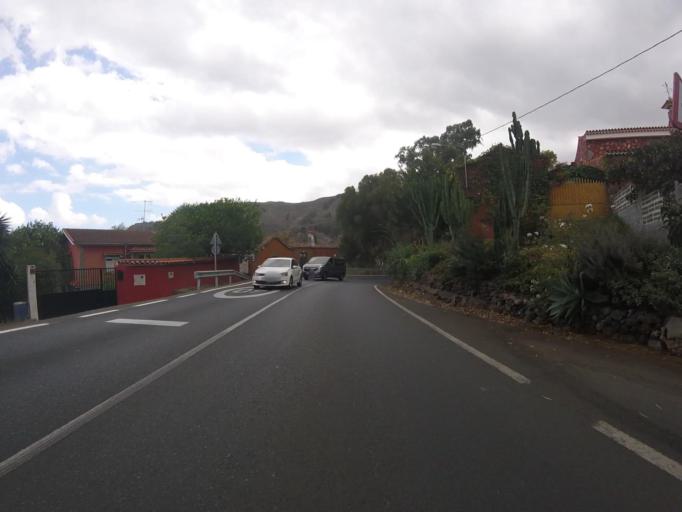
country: ES
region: Canary Islands
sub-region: Provincia de Las Palmas
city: Santa Brigida
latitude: 28.0269
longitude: -15.5046
